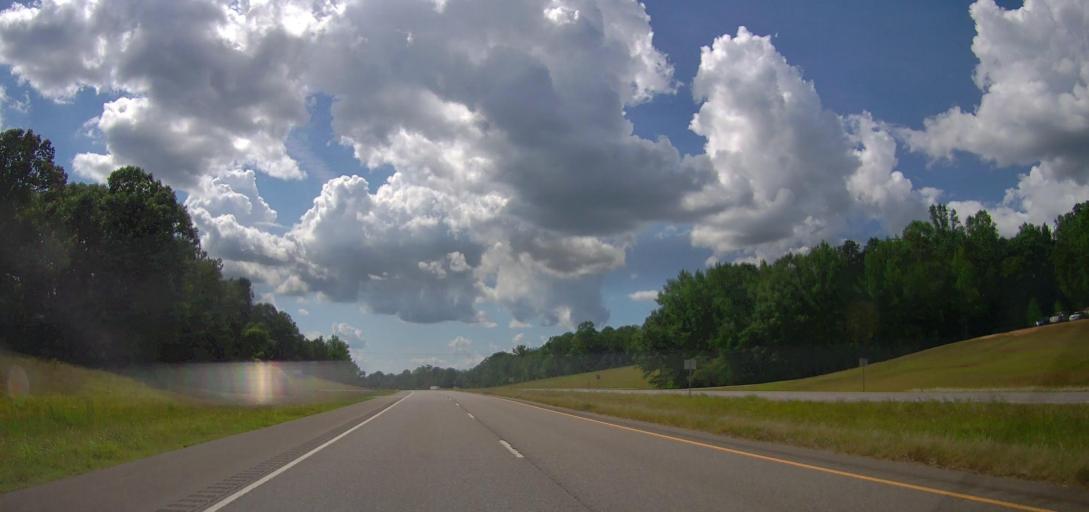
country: US
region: Alabama
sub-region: Pickens County
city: Reform
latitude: 33.4026
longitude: -88.0720
